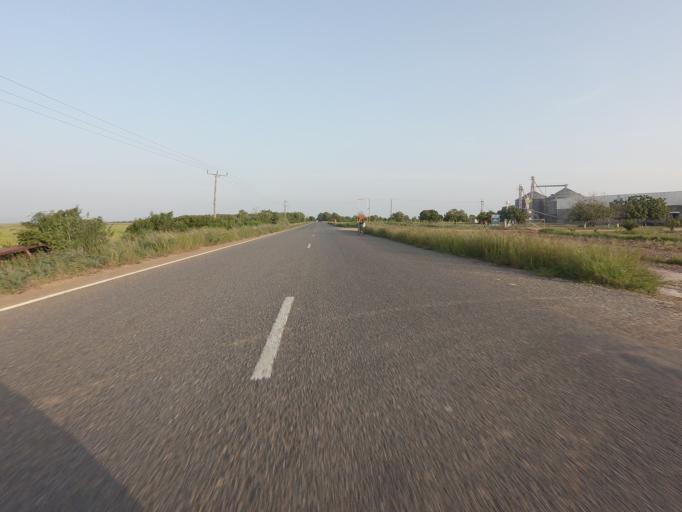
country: GH
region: Volta
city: Anloga
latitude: 5.9017
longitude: 0.7126
